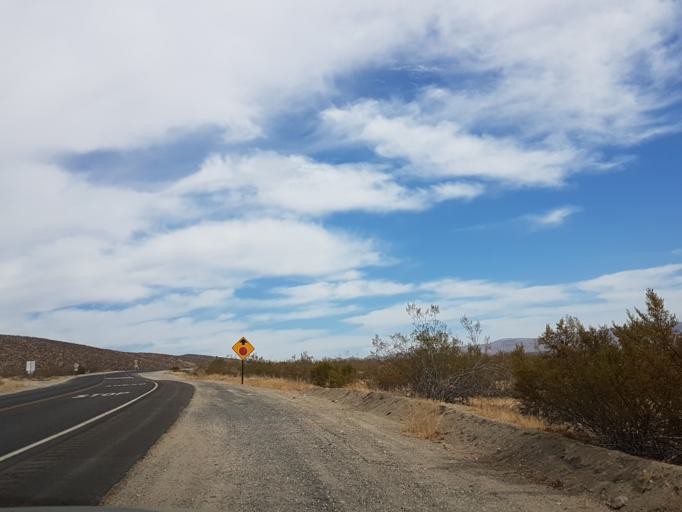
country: US
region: California
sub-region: Kern County
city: Ridgecrest
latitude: 35.4326
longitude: -117.6740
